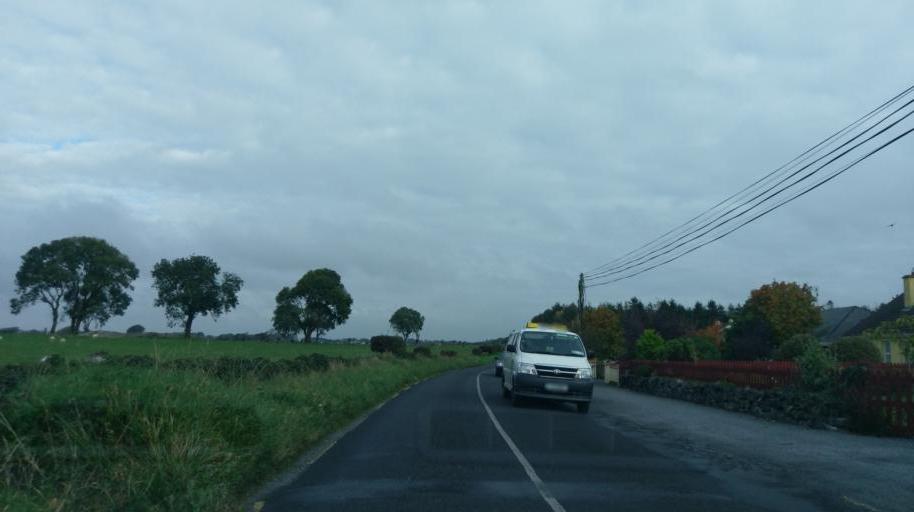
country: IE
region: Connaught
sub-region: County Galway
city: Athenry
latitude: 53.3523
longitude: -8.7067
